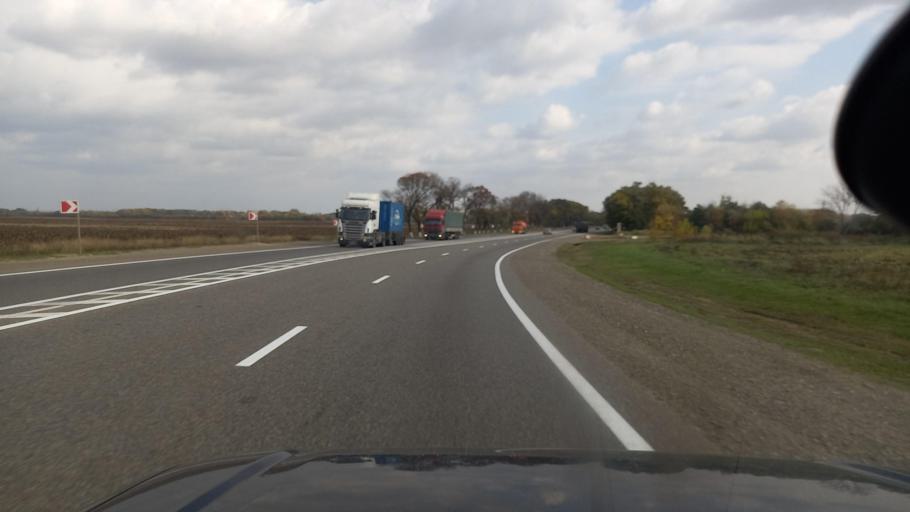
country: RU
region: Krasnodarskiy
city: Kholmskiy
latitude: 44.8501
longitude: 38.4335
